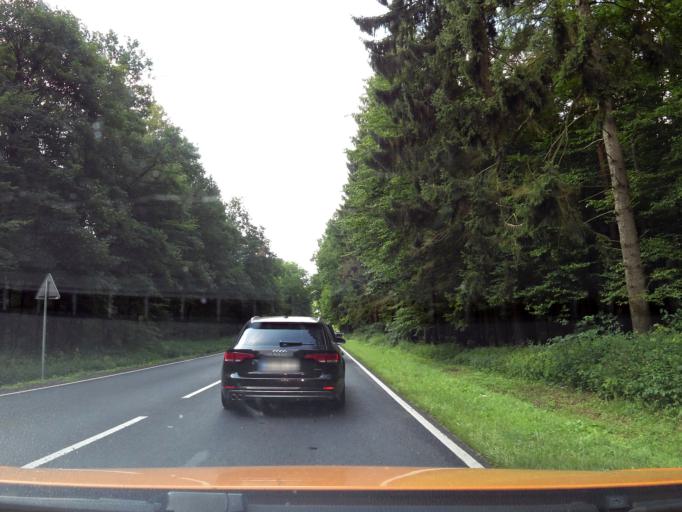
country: PL
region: West Pomeranian Voivodeship
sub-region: Powiat gryficki
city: Ploty
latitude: 53.8251
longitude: 15.2860
